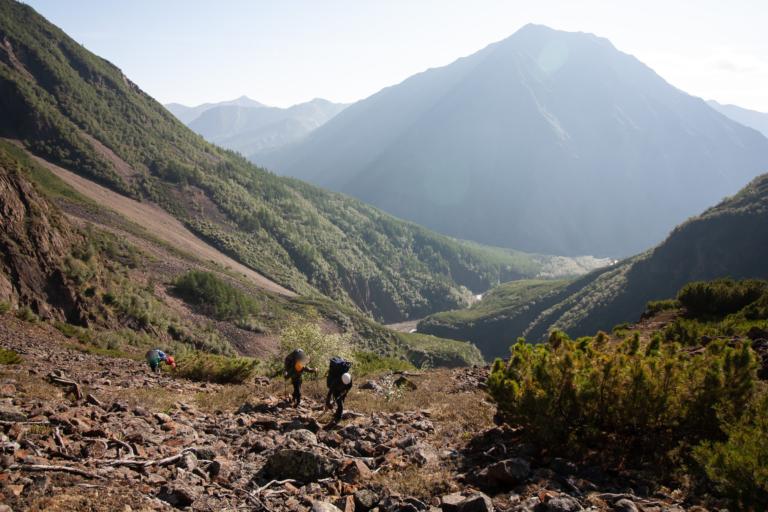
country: RU
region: Respublika Buryatiya
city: Novyy Uoyan
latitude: 56.2980
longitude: 111.3414
